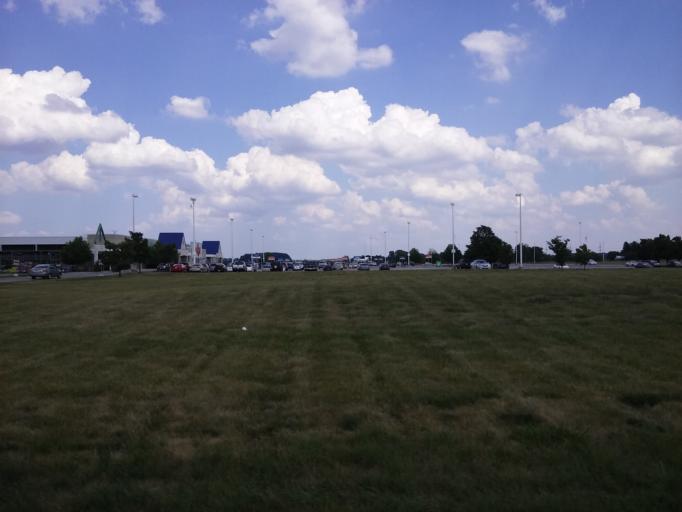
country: US
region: Ohio
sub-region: Wood County
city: Bowling Green
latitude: 41.3762
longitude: -83.6103
